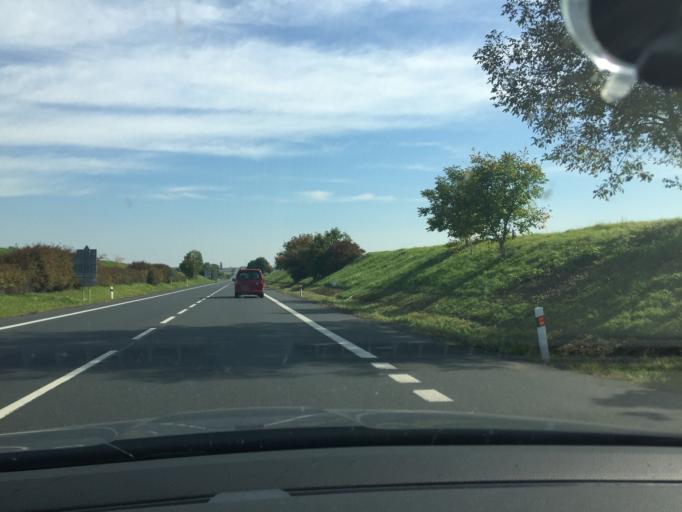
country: CZ
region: Central Bohemia
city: Planany
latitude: 50.0446
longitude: 15.0309
